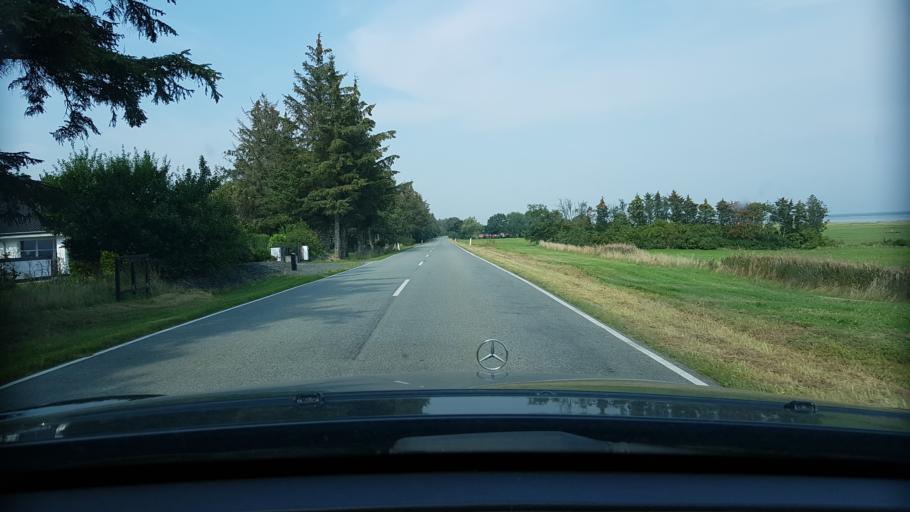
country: DK
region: North Denmark
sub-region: Alborg Kommune
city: Hals
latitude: 56.8750
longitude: 10.2610
